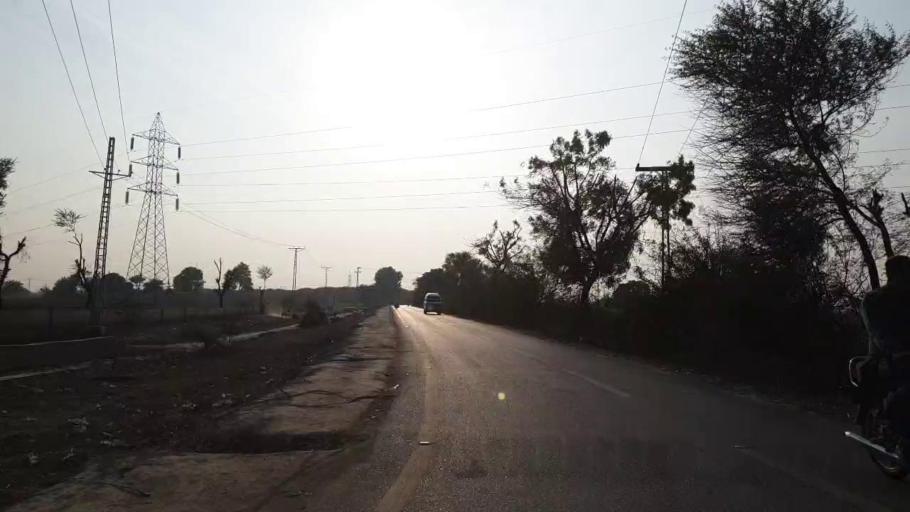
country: PK
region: Sindh
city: Matiari
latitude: 25.5865
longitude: 68.4509
